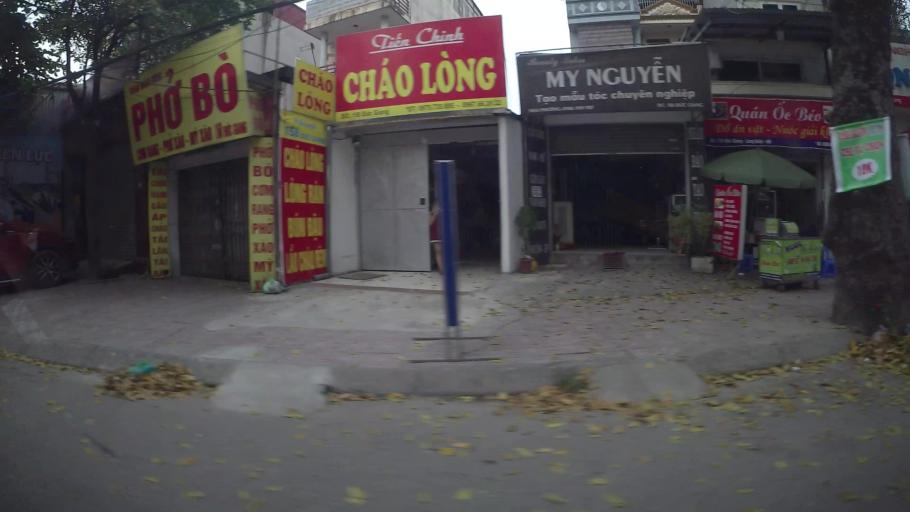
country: VN
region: Ha Noi
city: Hoan Kiem
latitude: 21.0672
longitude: 105.8839
